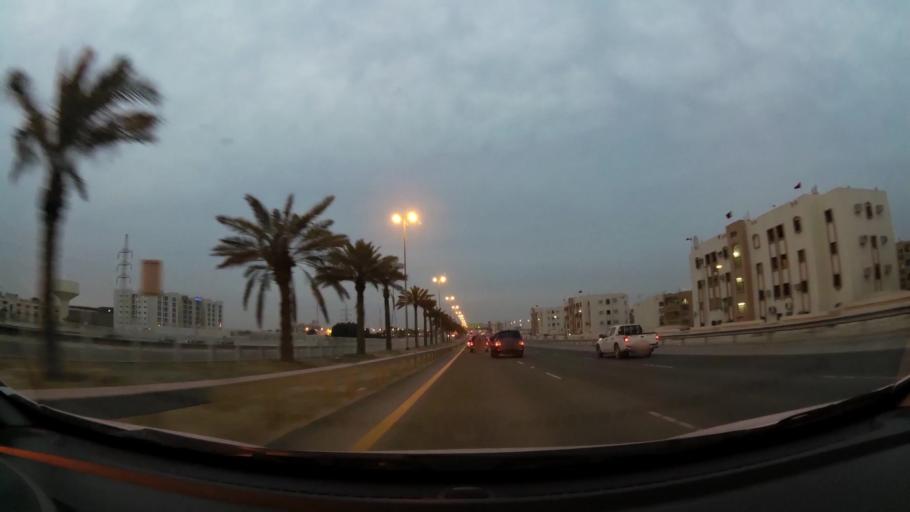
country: BH
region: Northern
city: Madinat `Isa
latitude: 26.1560
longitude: 50.5688
